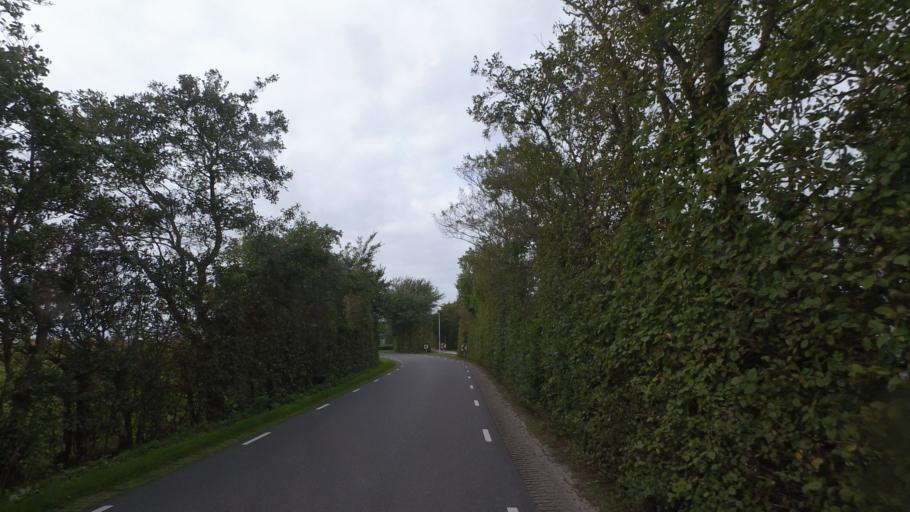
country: NL
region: Friesland
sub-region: Gemeente Ameland
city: Nes
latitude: 53.4465
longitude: 5.7905
